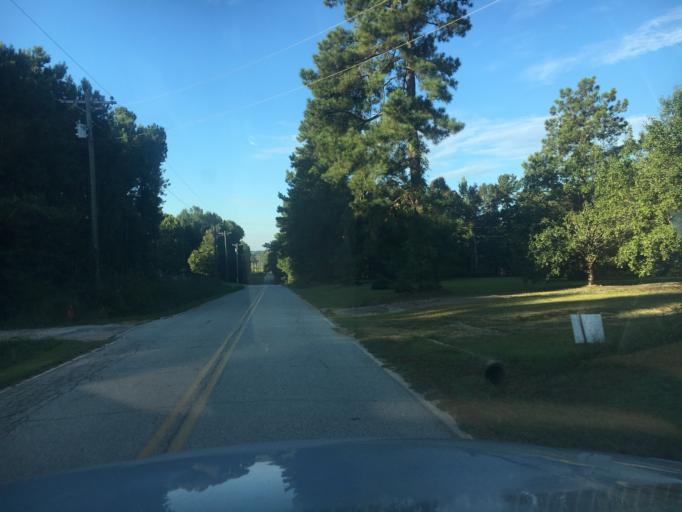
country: US
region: South Carolina
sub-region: Spartanburg County
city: Woodruff
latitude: 34.6891
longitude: -81.9571
